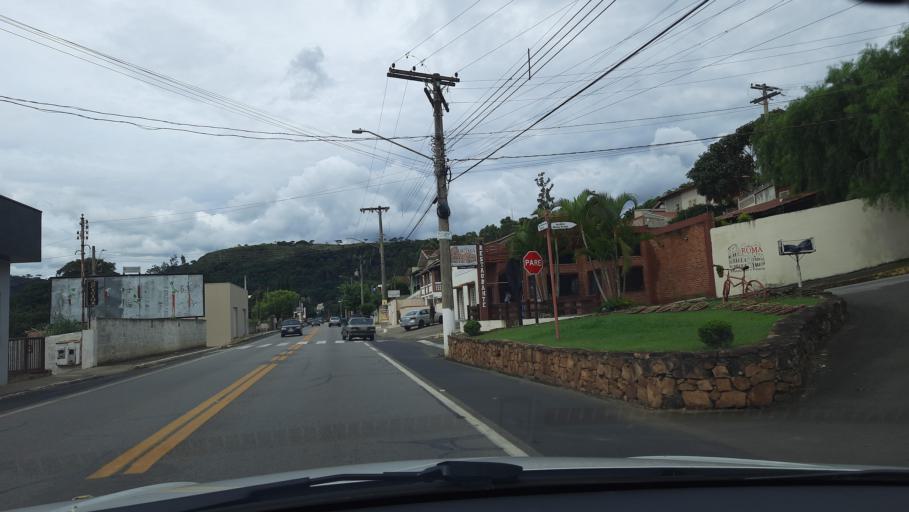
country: BR
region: Sao Paulo
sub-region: Sao Joao Da Boa Vista
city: Sao Joao da Boa Vista
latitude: -21.9474
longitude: -46.7189
